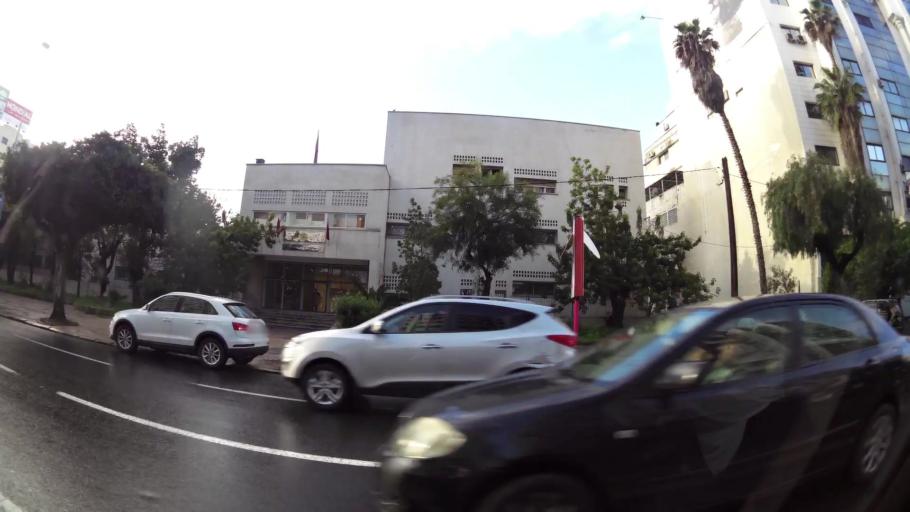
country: MA
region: Grand Casablanca
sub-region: Casablanca
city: Casablanca
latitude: 33.5827
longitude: -7.6189
